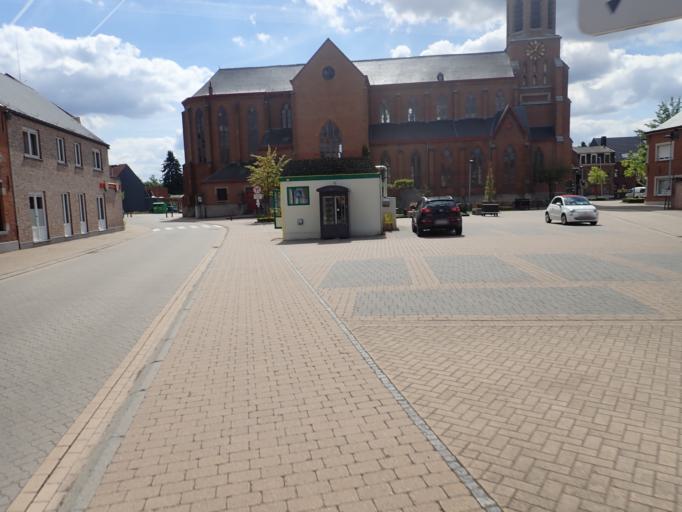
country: BE
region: Flanders
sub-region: Provincie Antwerpen
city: Hulshout
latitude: 51.0535
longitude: 4.7787
